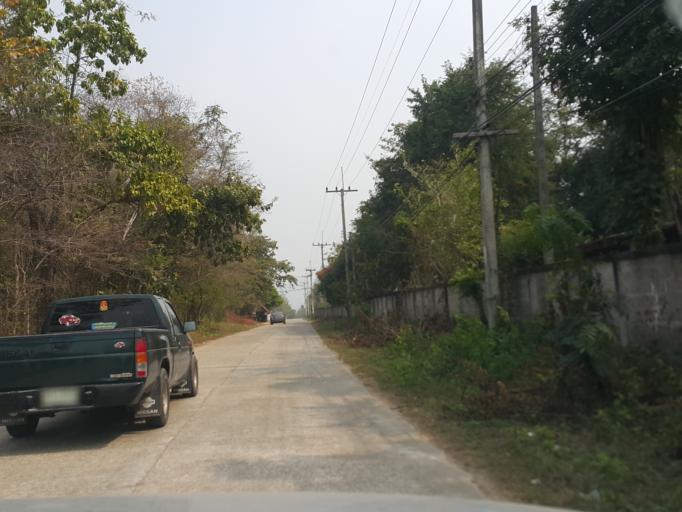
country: TH
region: Lampang
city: Thoen
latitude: 17.6365
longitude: 99.2417
